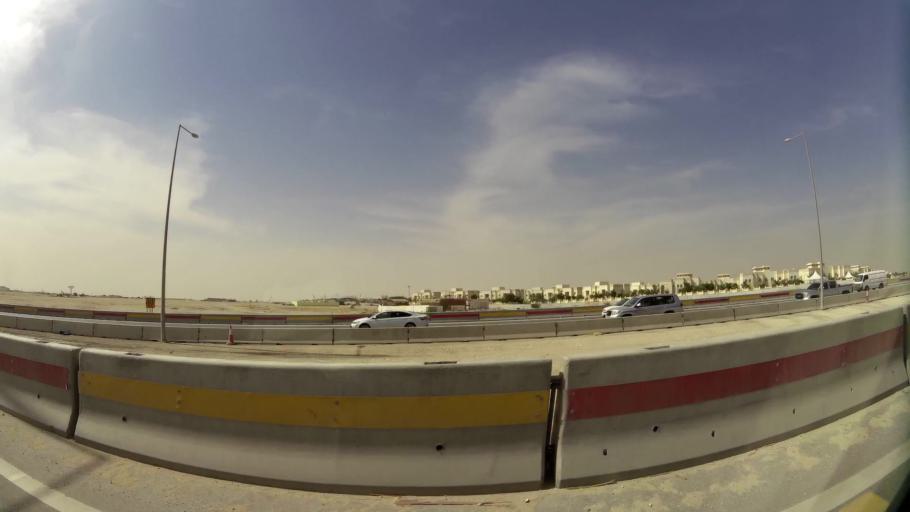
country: QA
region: Baladiyat ar Rayyan
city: Ar Rayyan
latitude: 25.3191
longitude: 51.4197
